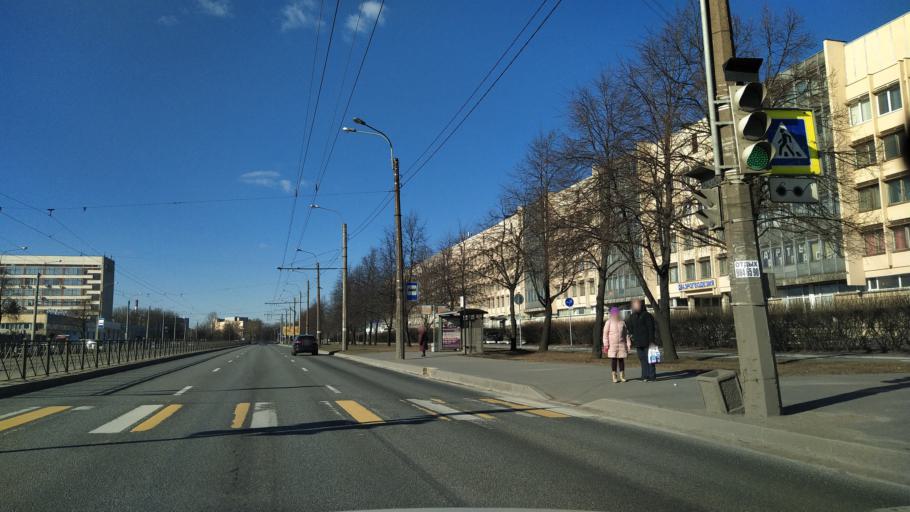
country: RU
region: St.-Petersburg
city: Kupchino
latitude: 59.8906
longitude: 30.3606
